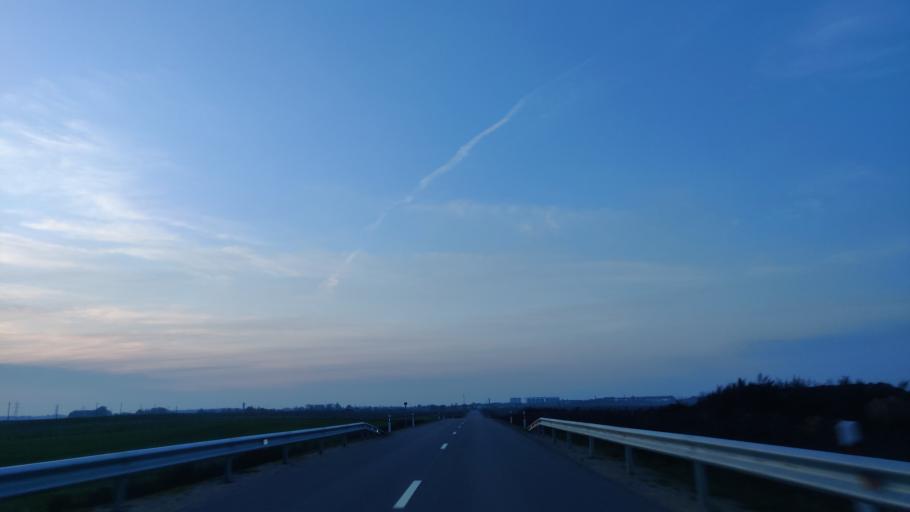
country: LT
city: Lentvaris
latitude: 54.6028
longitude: 25.0056
